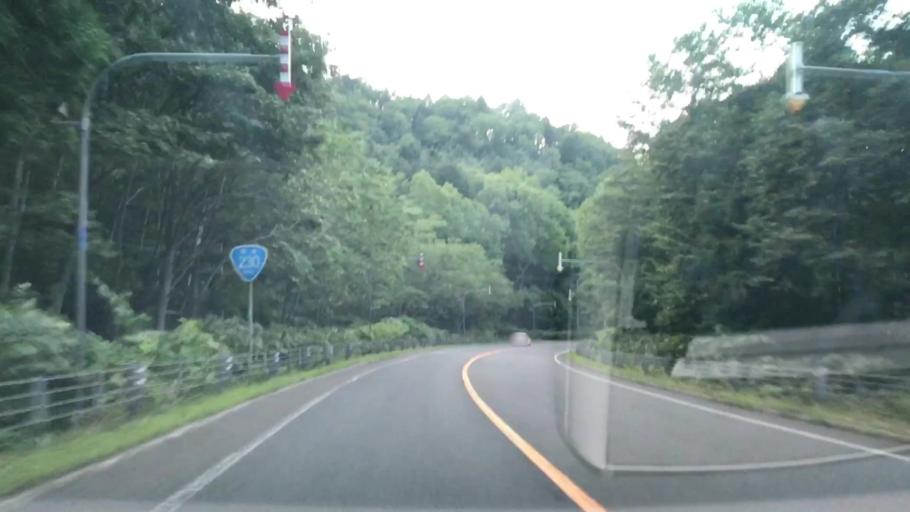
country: JP
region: Hokkaido
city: Sapporo
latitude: 42.9220
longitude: 141.1232
